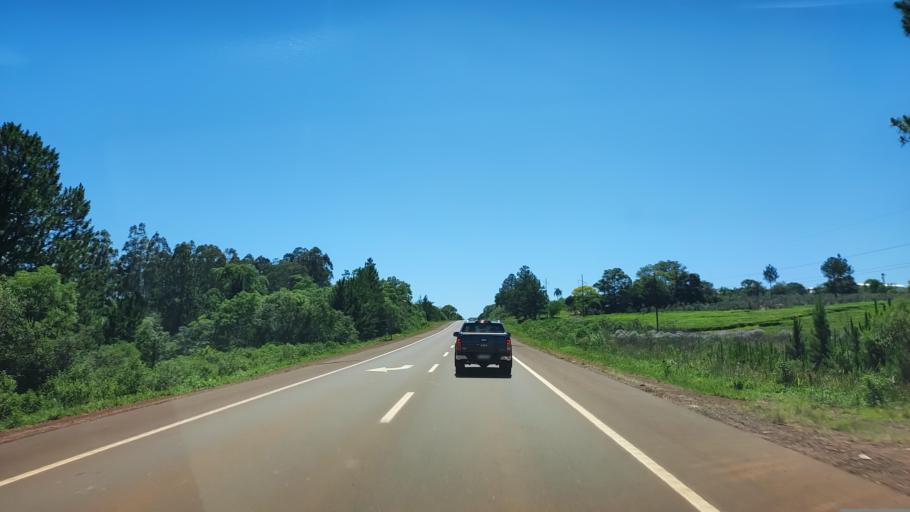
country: AR
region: Misiones
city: Aristobulo del Valle
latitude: -27.0866
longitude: -54.7831
